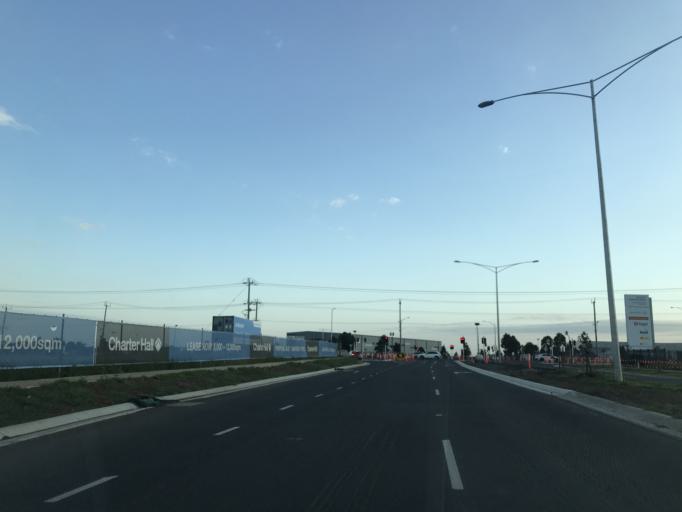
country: AU
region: Victoria
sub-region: Hobsons Bay
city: Laverton
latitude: -37.8394
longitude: 144.7621
